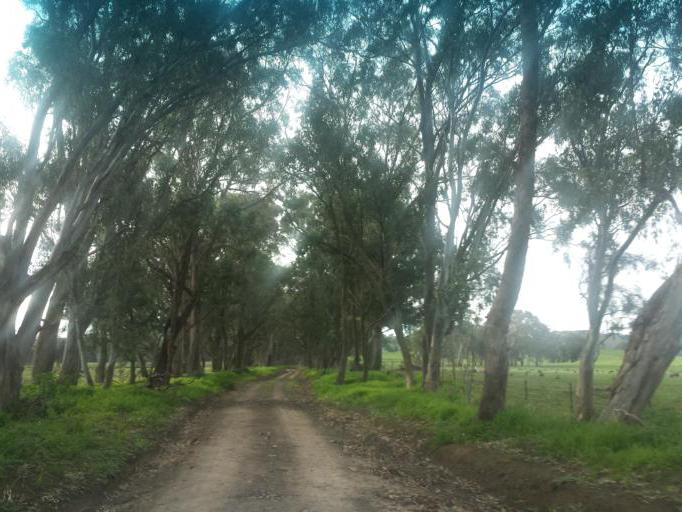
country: AU
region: Victoria
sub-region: Murrindindi
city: Kinglake West
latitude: -37.0220
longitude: 145.2502
